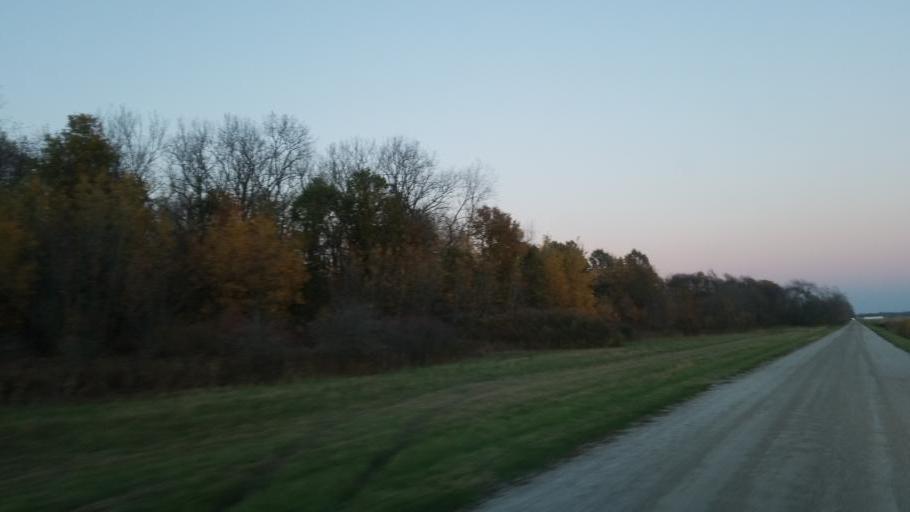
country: US
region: Ohio
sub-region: Huron County
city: Willard
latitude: 40.9959
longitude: -82.7750
